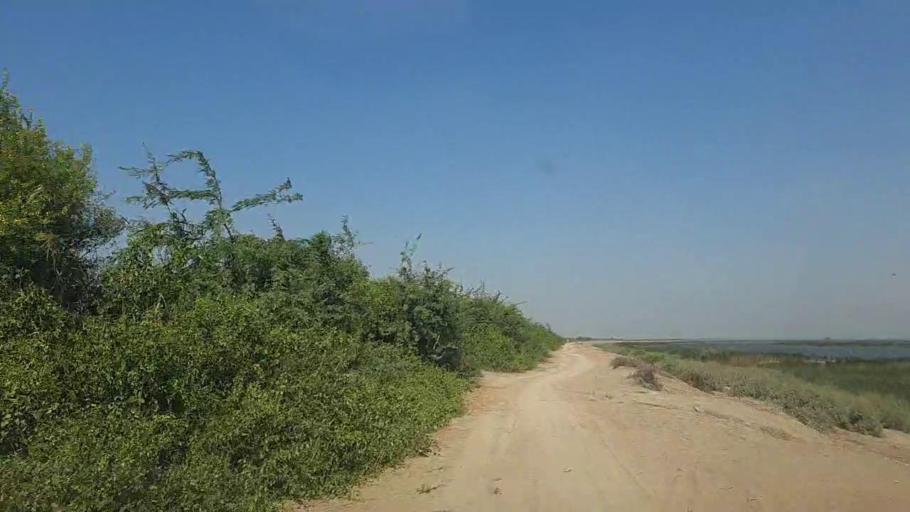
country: PK
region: Sindh
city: Daro Mehar
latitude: 24.9171
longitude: 68.0784
